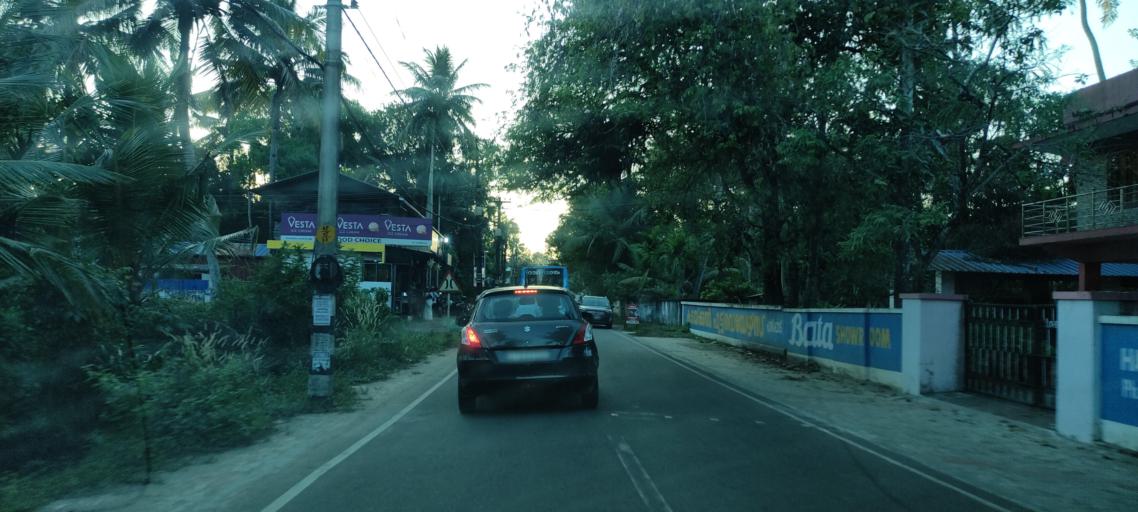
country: IN
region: Kerala
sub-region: Alappuzha
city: Kayankulam
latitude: 9.2596
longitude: 76.4425
